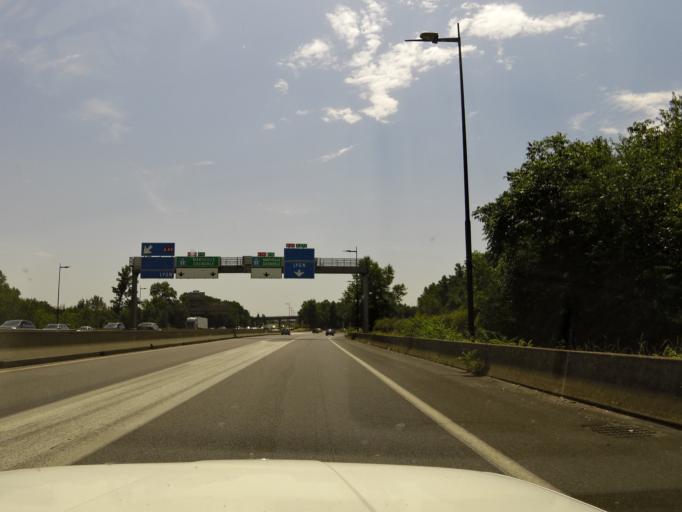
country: FR
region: Rhone-Alpes
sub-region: Departement du Rhone
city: Vaulx-en-Velin
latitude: 45.8015
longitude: 4.9273
